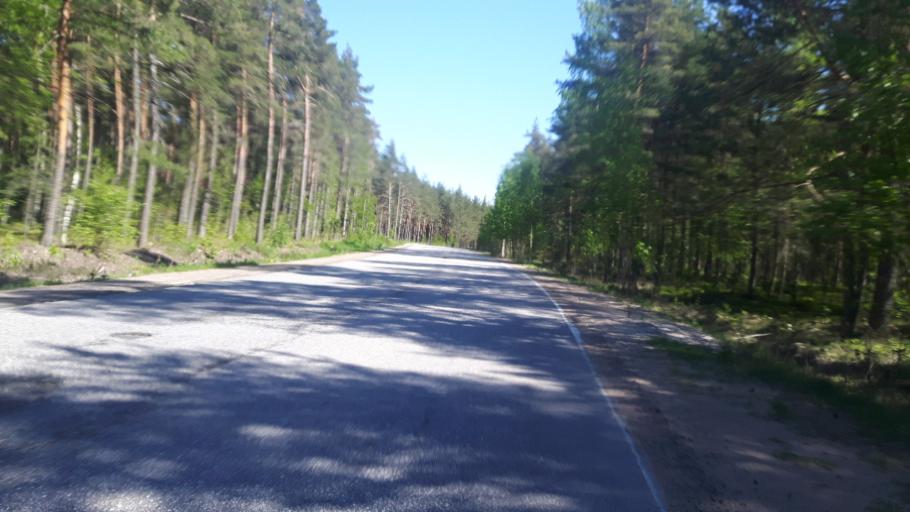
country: RU
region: Leningrad
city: Glebychevo
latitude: 60.2794
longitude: 28.8923
